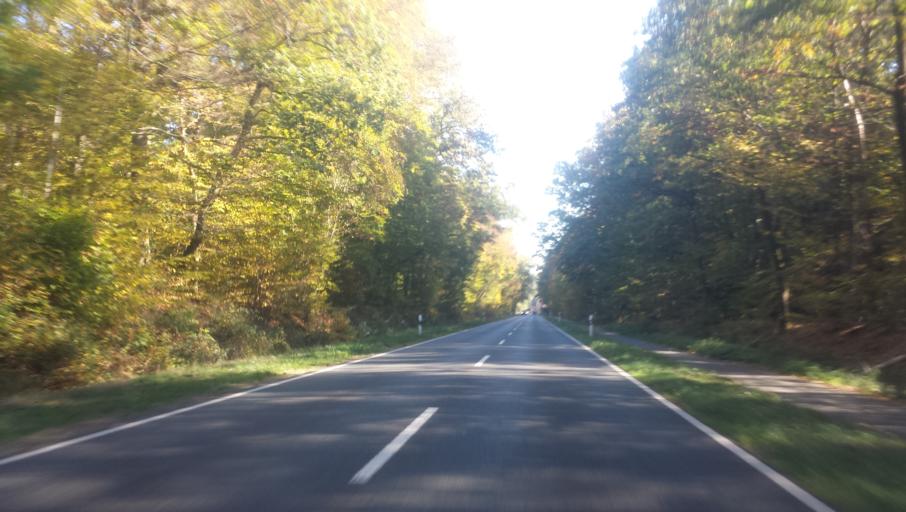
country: DE
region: Hesse
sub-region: Regierungsbezirk Darmstadt
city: Messel
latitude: 49.9043
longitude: 8.7390
